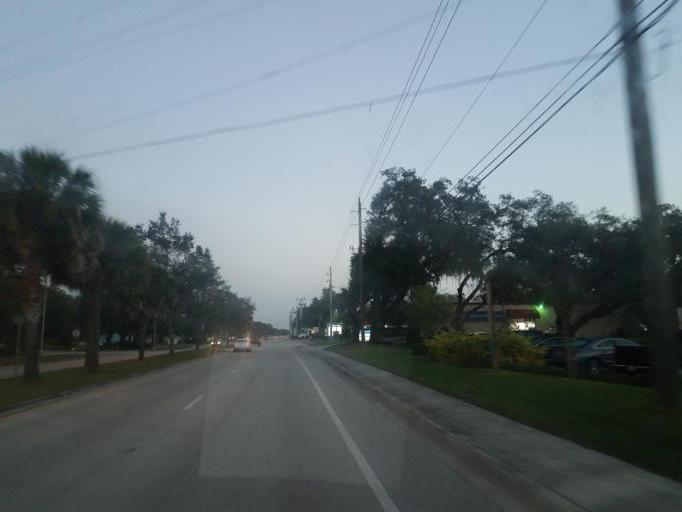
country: US
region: Florida
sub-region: Sarasota County
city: Fruitville
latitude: 27.3126
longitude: -82.4513
